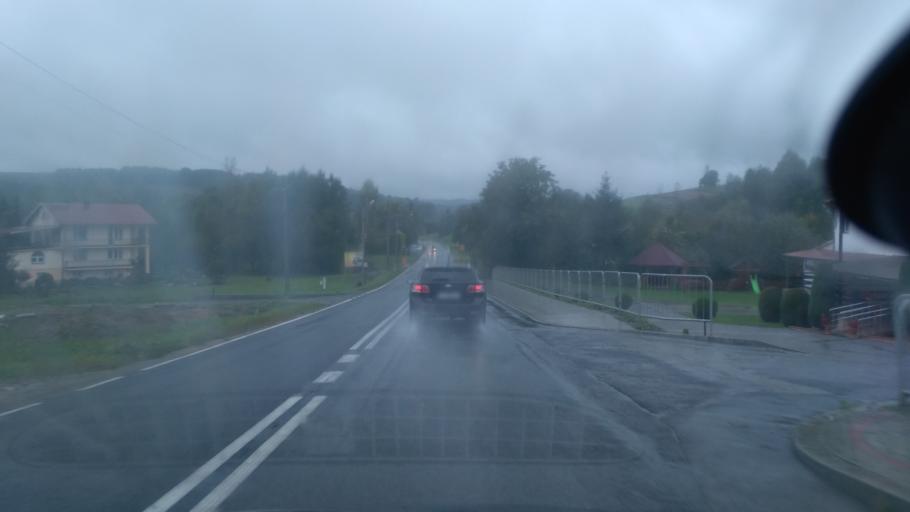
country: PL
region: Subcarpathian Voivodeship
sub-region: Powiat ropczycko-sedziszowski
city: Niedzwiada
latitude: 50.0035
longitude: 21.5589
